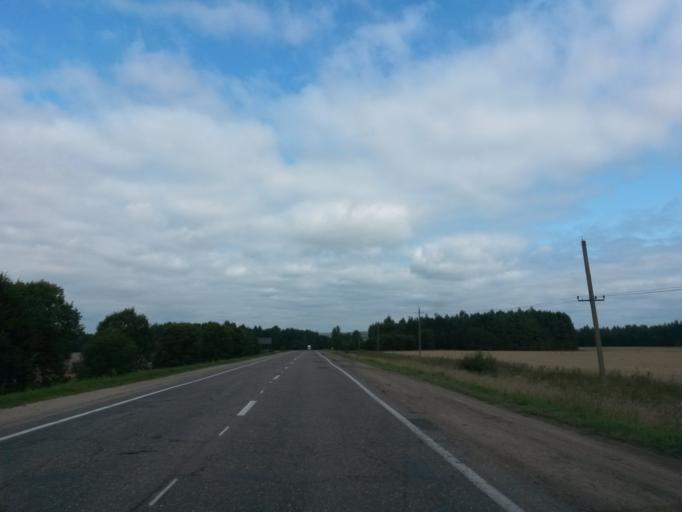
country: RU
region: Jaroslavl
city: Gavrilov-Yam
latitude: 57.3115
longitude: 39.9359
